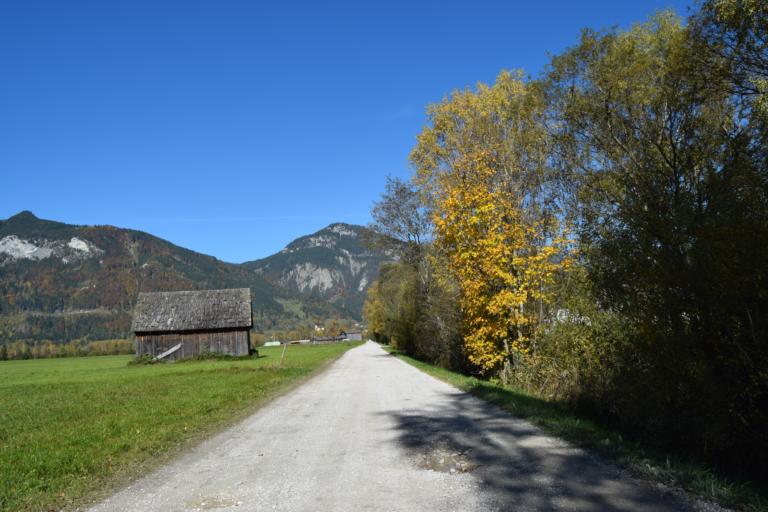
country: AT
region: Styria
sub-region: Politischer Bezirk Liezen
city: Irdning
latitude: 47.5133
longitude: 14.1048
